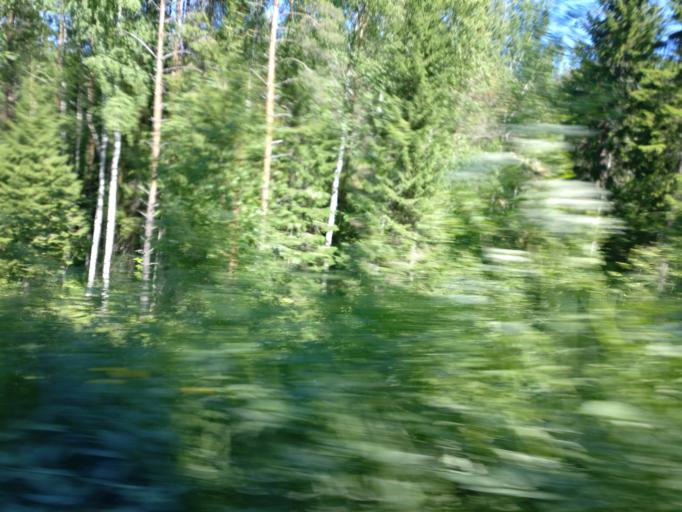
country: FI
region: Southern Savonia
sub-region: Savonlinna
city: Rantasalmi
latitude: 62.1482
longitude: 28.2429
